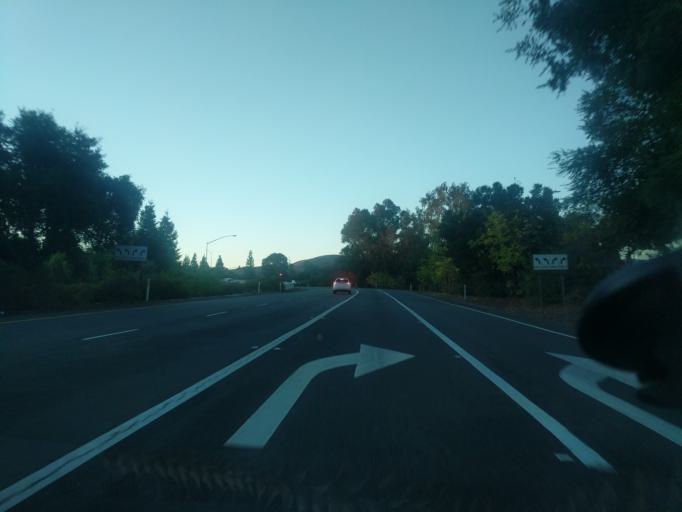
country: US
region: California
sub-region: Contra Costa County
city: San Ramon
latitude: 37.7783
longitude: -121.9768
